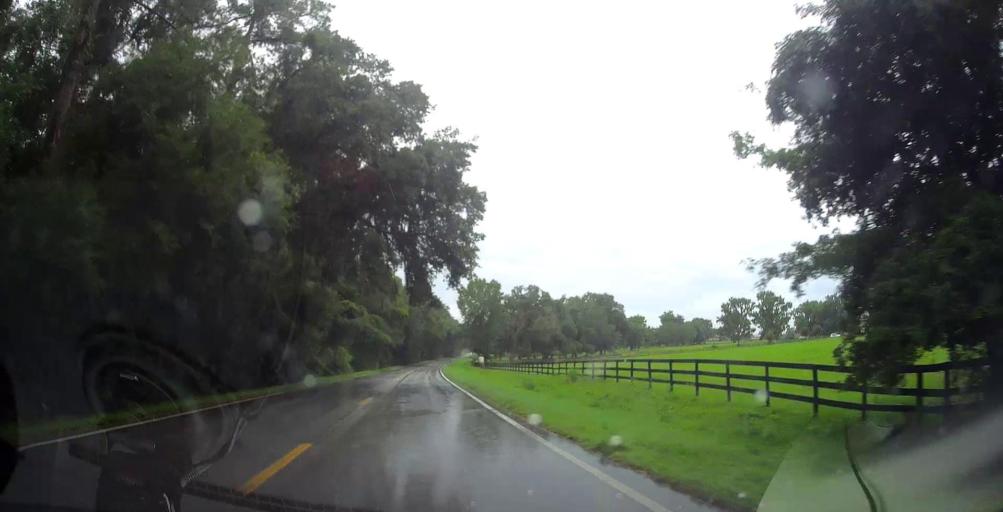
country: US
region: Florida
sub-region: Marion County
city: Citra
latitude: 29.3399
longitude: -82.2118
